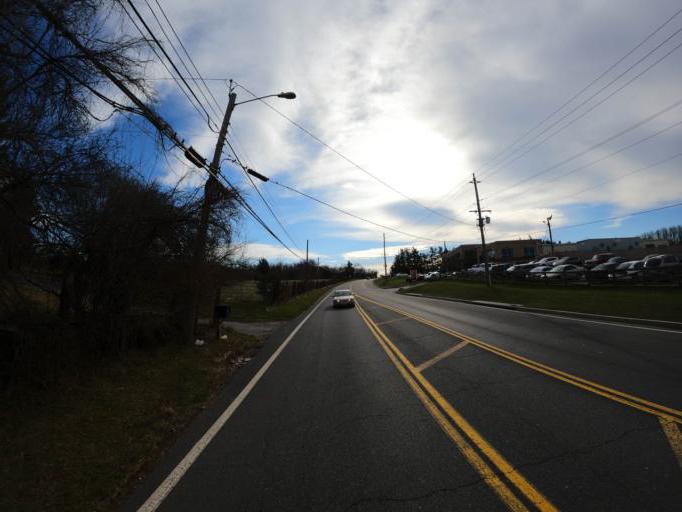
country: US
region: Maryland
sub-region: Montgomery County
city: Clarksburg
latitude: 39.2518
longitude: -77.2990
